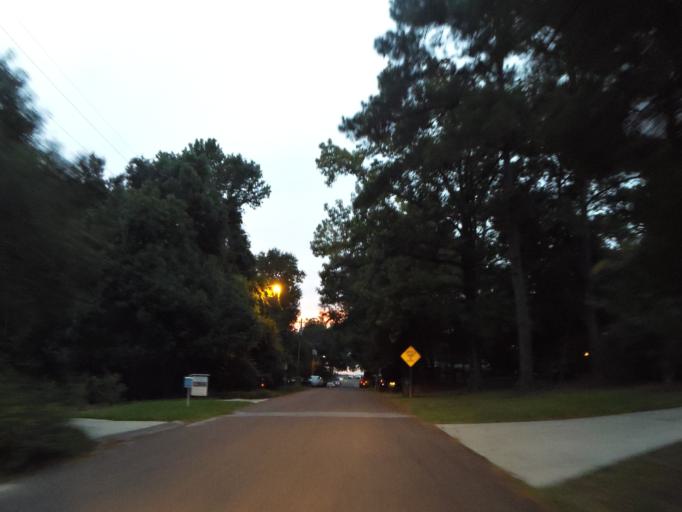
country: US
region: Alabama
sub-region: Baldwin County
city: Fairhope
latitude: 30.5406
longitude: -87.9015
